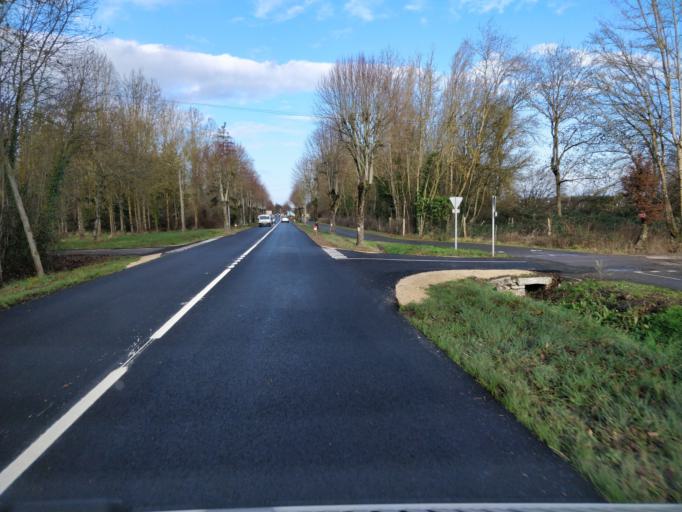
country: FR
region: Centre
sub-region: Departement du Loir-et-Cher
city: Mer
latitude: 47.6882
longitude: 1.5158
